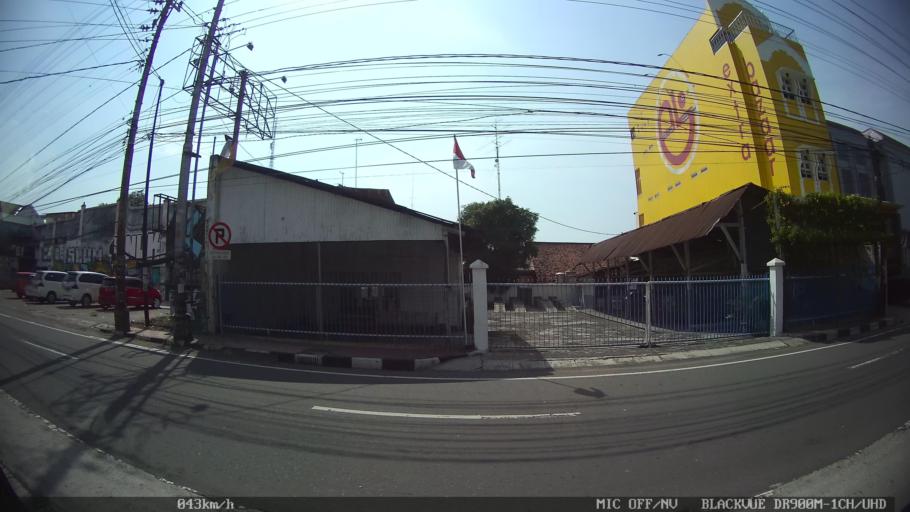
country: ID
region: Daerah Istimewa Yogyakarta
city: Yogyakarta
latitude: -7.7986
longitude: 110.3701
